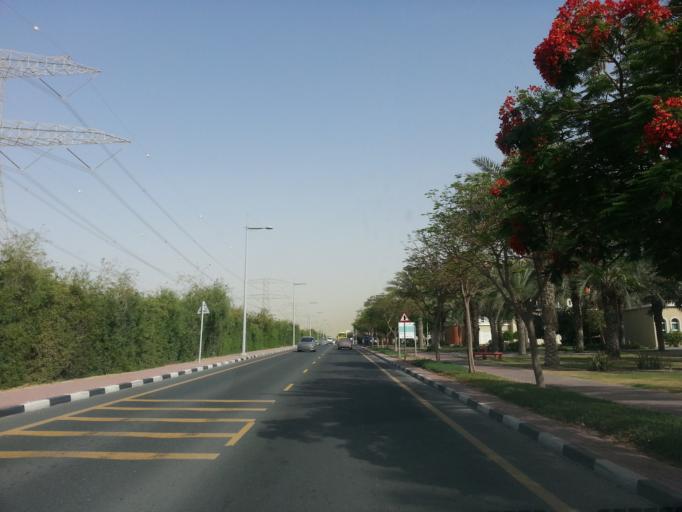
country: AE
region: Dubai
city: Dubai
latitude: 25.0433
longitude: 55.1435
